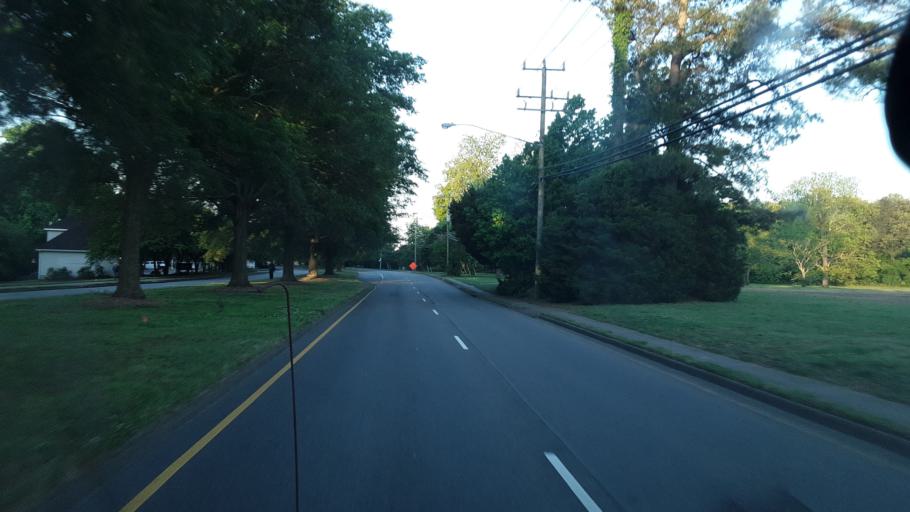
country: US
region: Virginia
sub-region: City of Virginia Beach
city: Virginia Beach
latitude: 36.7727
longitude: -76.0098
